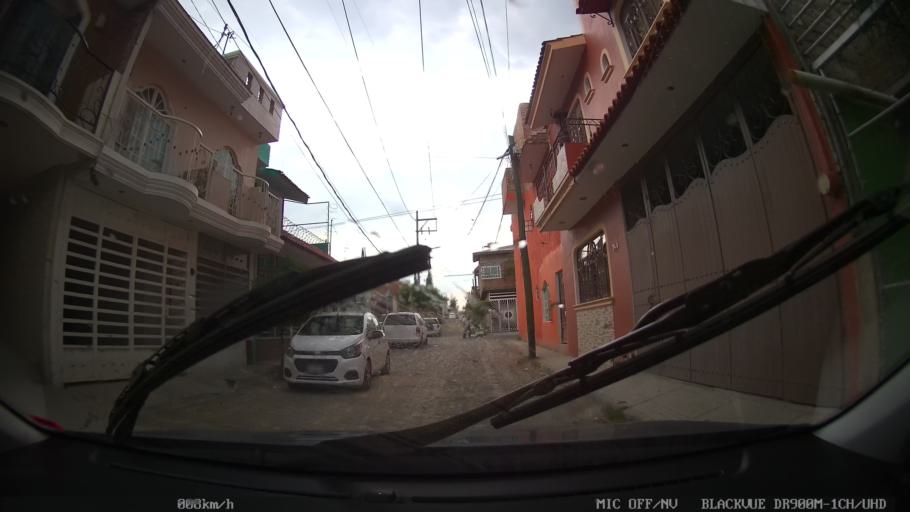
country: MX
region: Jalisco
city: Tlaquepaque
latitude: 20.6252
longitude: -103.2725
